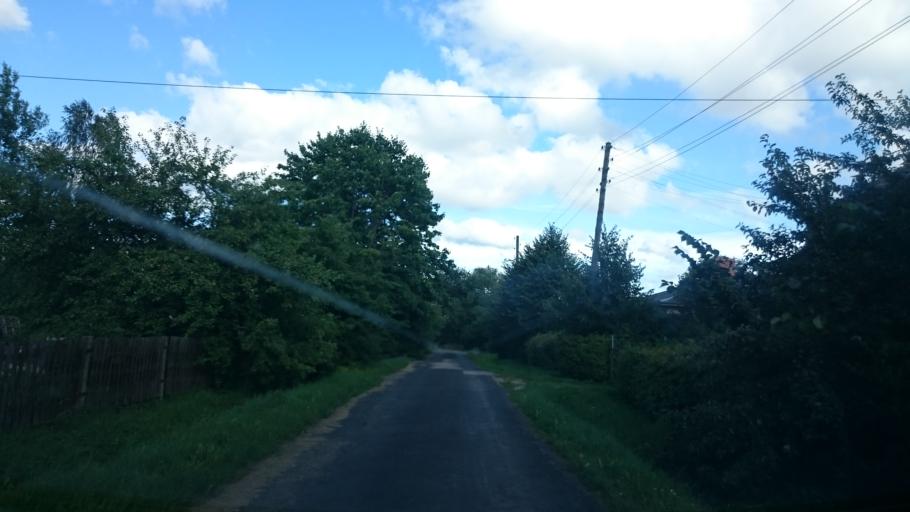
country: LV
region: Aizpute
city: Aizpute
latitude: 56.7164
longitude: 21.6195
